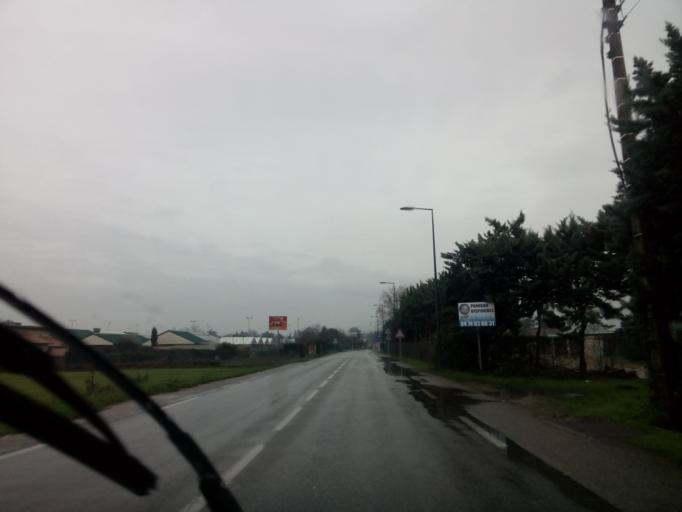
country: FR
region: Rhone-Alpes
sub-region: Departement de la Drome
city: Romans-sur-Isere
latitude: 45.0434
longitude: 5.0264
